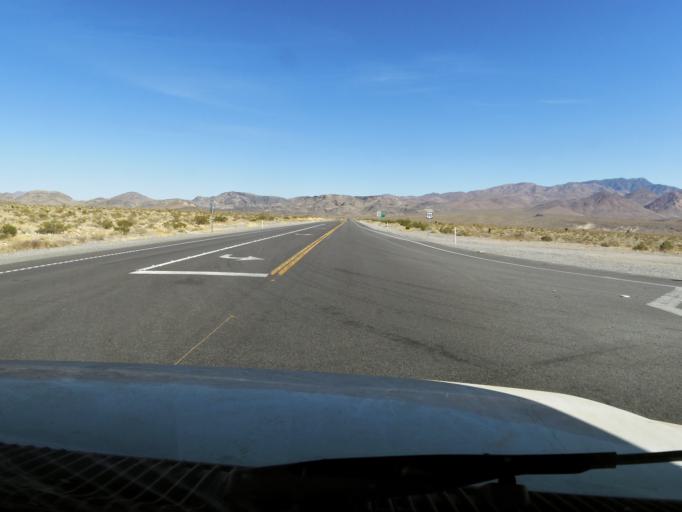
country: US
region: Nevada
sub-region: Nye County
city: Pahrump
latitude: 36.5648
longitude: -116.1233
